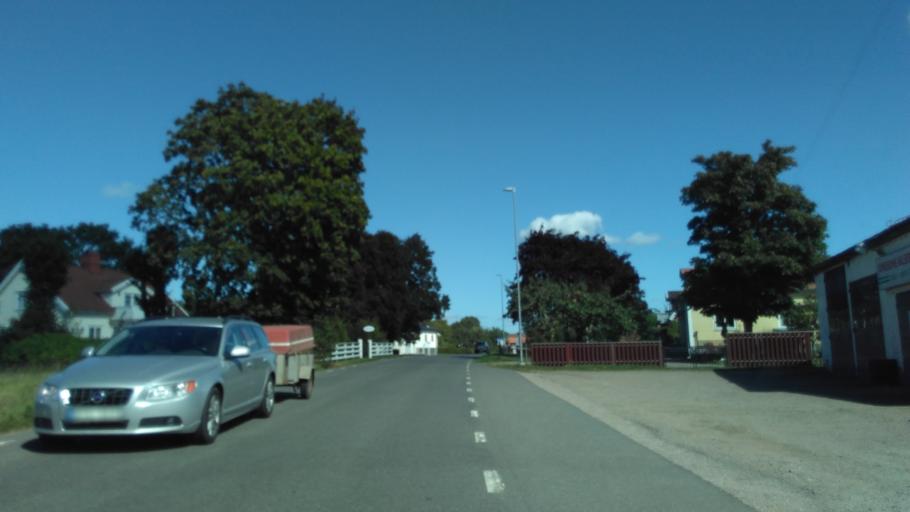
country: SE
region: Vaestra Goetaland
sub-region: Skara Kommun
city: Axvall
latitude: 58.4328
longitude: 13.6421
